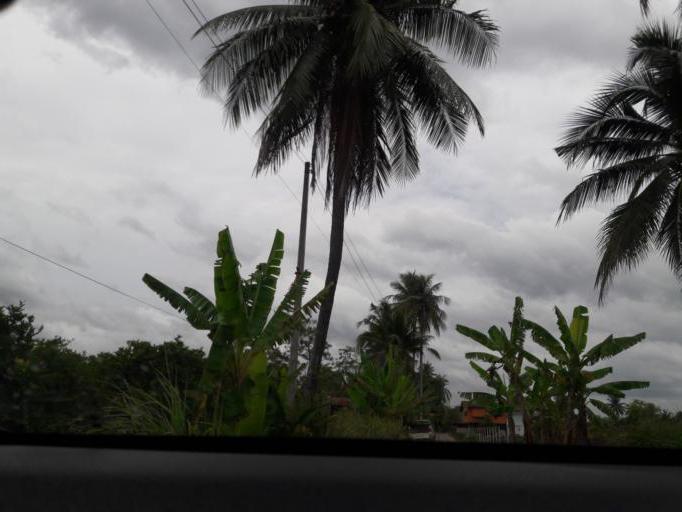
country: TH
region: Ratchaburi
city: Damnoen Saduak
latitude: 13.5702
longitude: 99.9956
